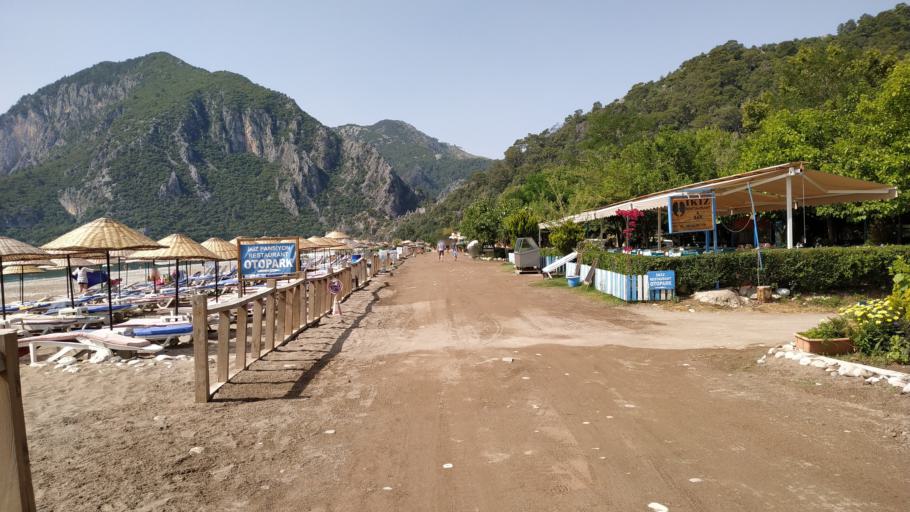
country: TR
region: Antalya
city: Tekirova
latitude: 36.4036
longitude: 30.4774
